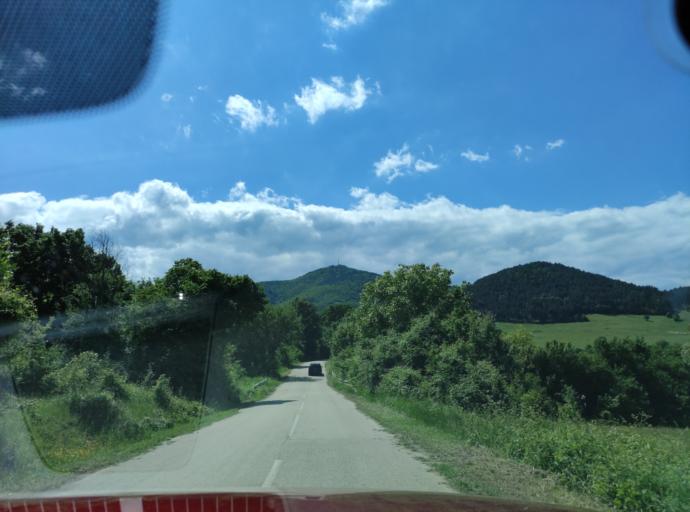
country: BG
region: Vidin
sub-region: Obshtina Ruzhintsi
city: Ruzhintsi
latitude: 43.5017
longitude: 22.7564
